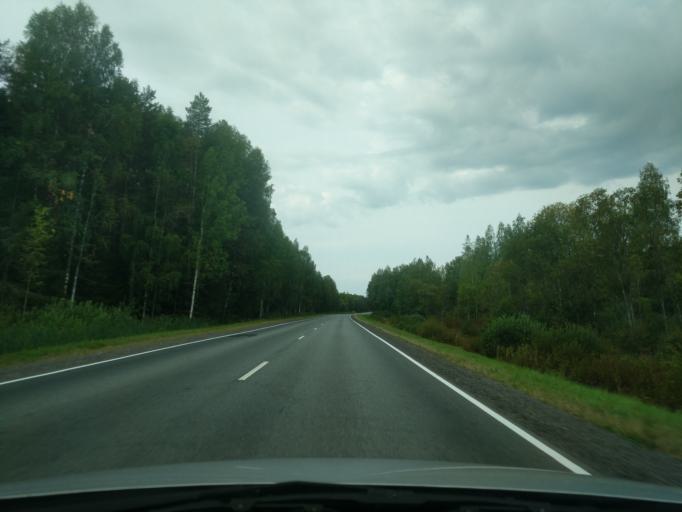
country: RU
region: Kirov
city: Svecha
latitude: 58.2704
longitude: 47.7172
